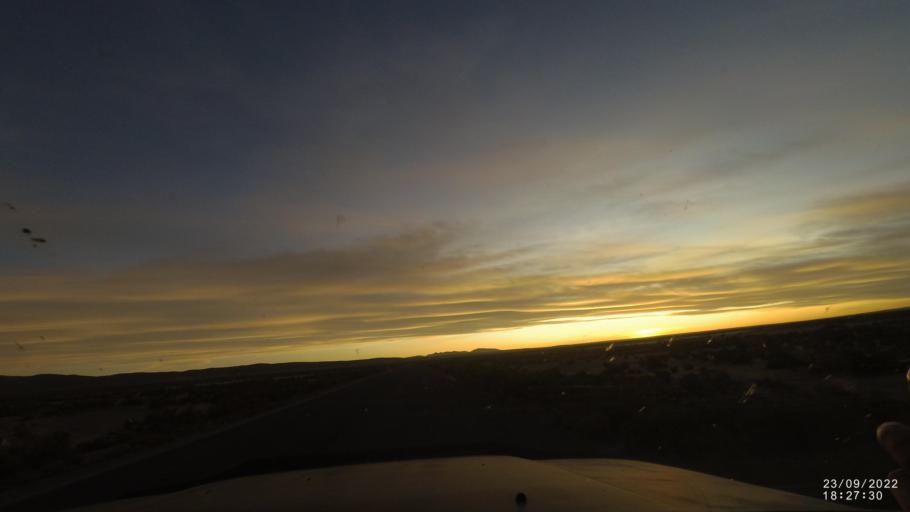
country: BO
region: Oruro
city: Challapata
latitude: -19.3288
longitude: -67.1684
